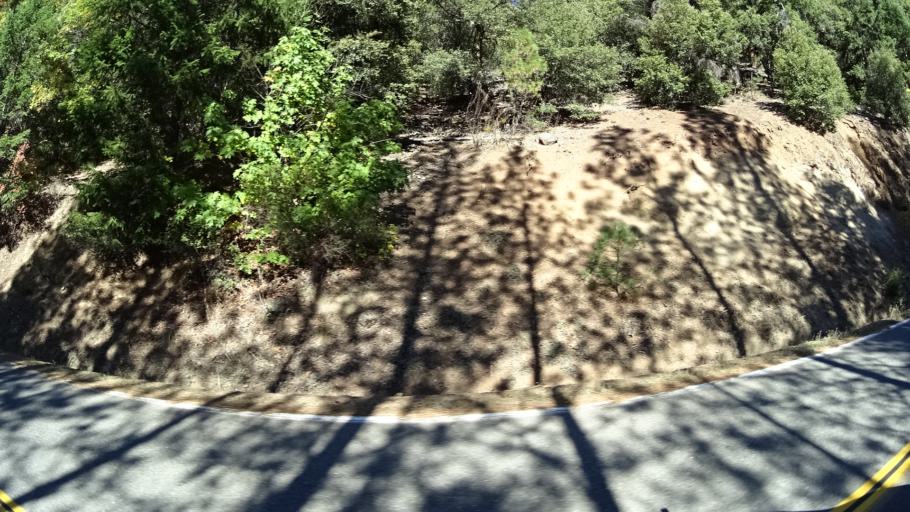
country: US
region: California
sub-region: Trinity County
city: Weaverville
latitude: 41.2105
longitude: -123.0471
